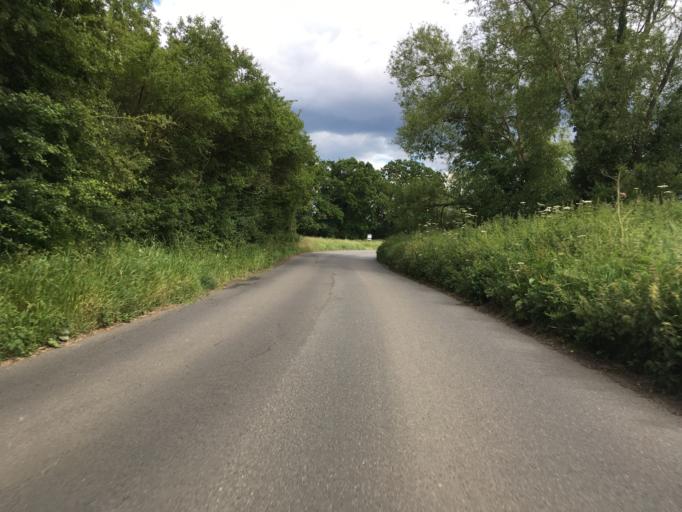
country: GB
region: England
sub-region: Wiltshire
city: Cricklade
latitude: 51.6228
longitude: -1.8553
